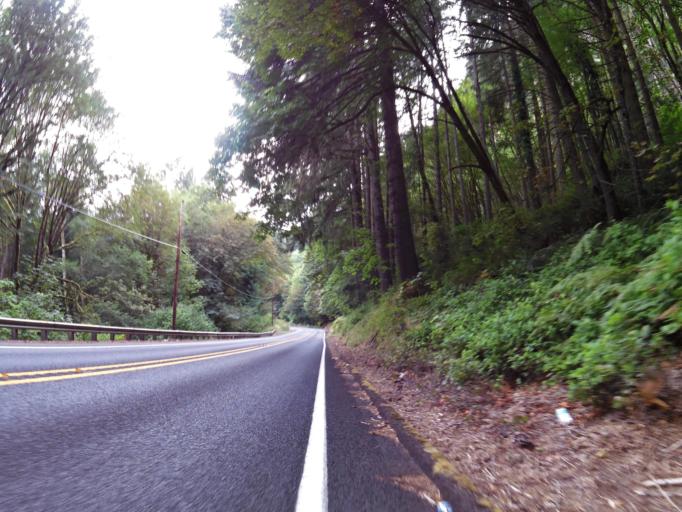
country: US
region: Oregon
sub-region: Columbia County
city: Clatskanie
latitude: 46.1737
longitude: -123.2242
